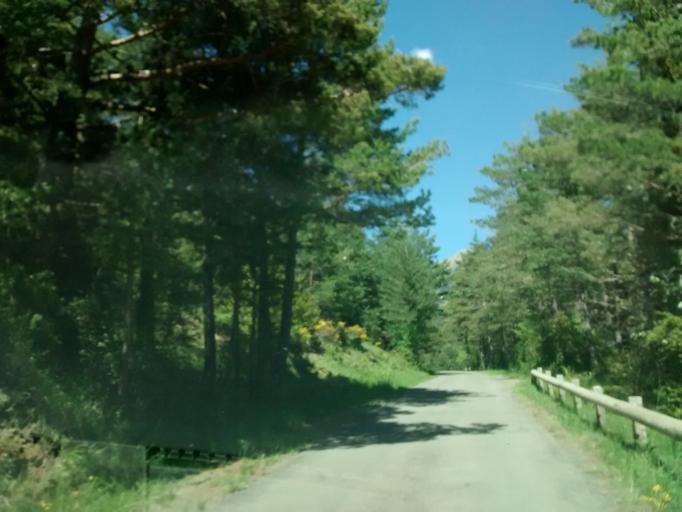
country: ES
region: Aragon
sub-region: Provincia de Huesca
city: Borau
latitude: 42.7143
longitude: -0.6065
